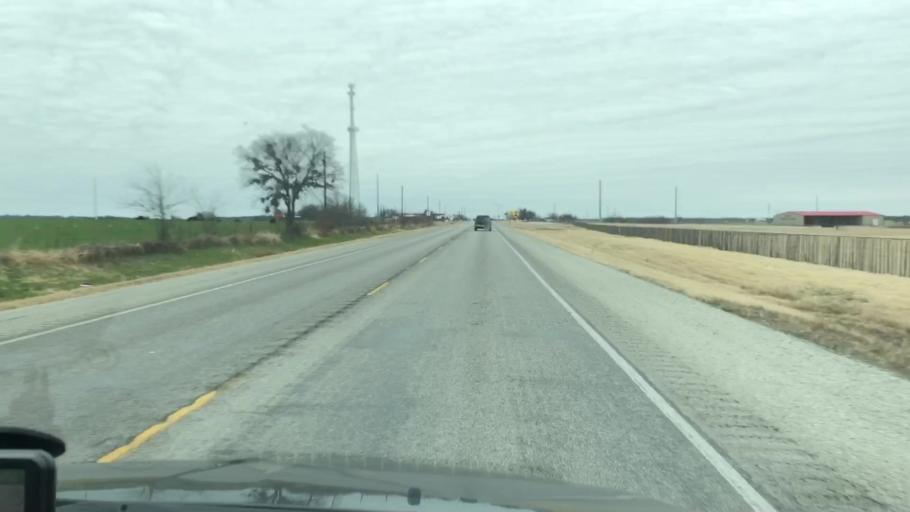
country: US
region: Texas
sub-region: Palo Pinto County
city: Mineral Wells
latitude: 32.9158
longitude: -98.0770
